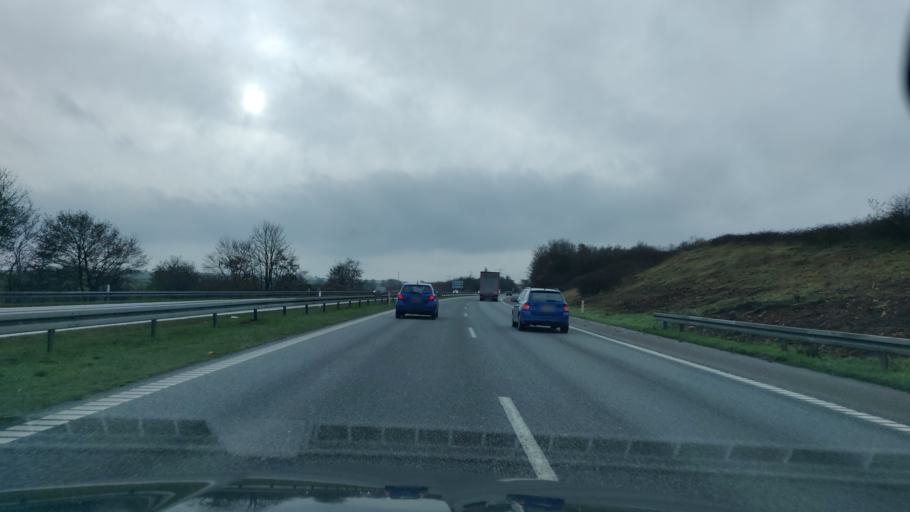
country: DK
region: North Denmark
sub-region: Alborg Kommune
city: Aalborg
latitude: 56.9961
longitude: 9.9048
